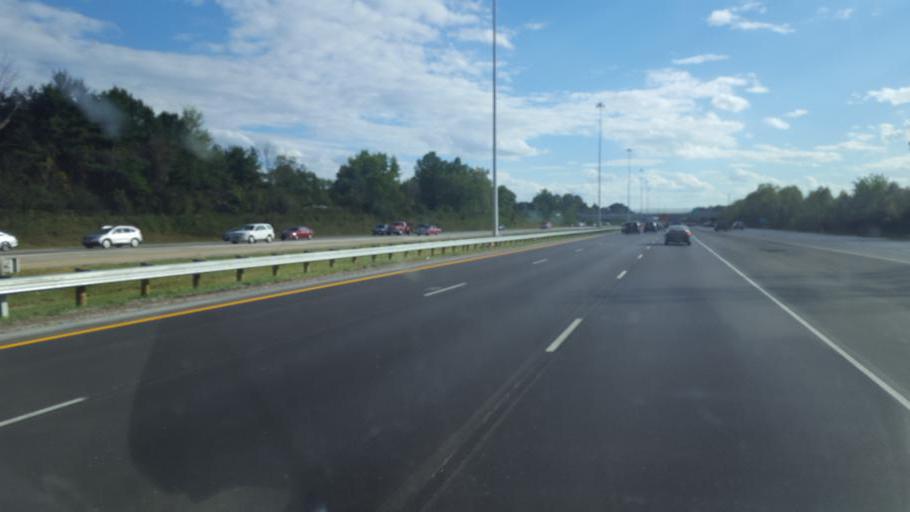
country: US
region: Ohio
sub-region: Franklin County
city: Gahanna
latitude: 40.0373
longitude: -82.9031
